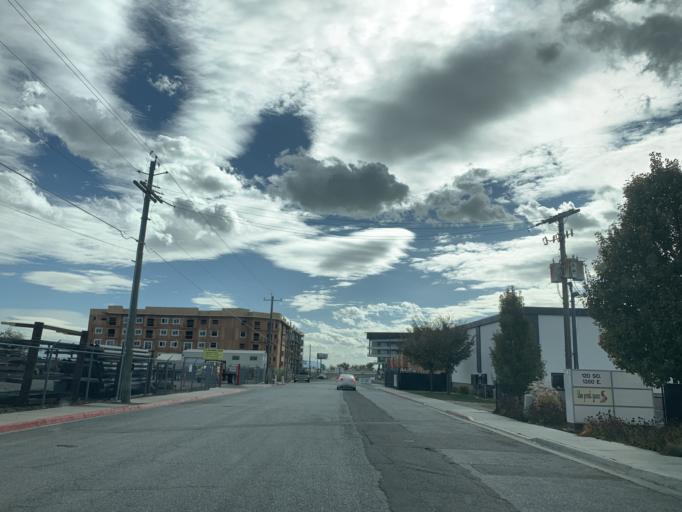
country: US
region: Utah
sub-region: Utah County
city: Lehi
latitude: 40.3869
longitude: -111.8292
